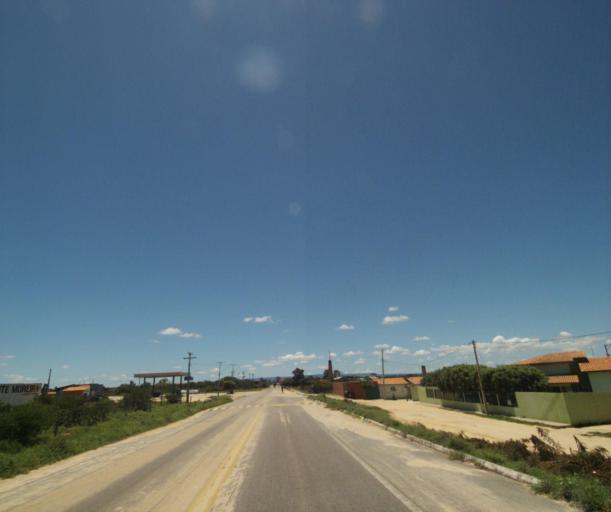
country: BR
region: Bahia
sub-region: Carinhanha
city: Carinhanha
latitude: -14.2911
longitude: -43.7782
